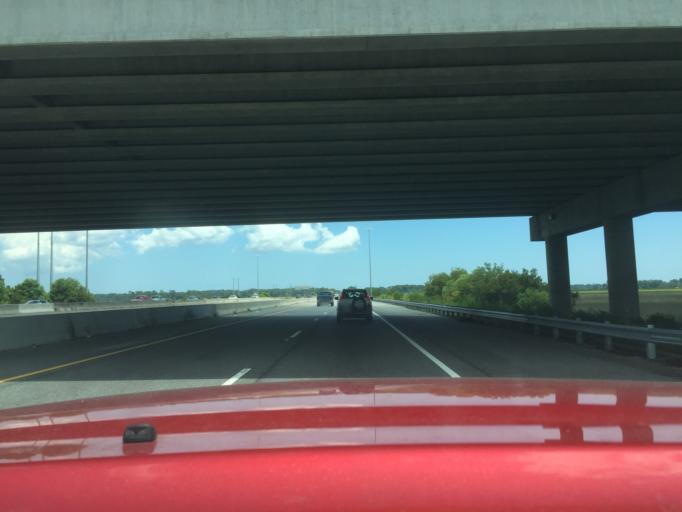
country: US
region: Georgia
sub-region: Chatham County
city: Georgetown
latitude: 31.9842
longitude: -81.2002
